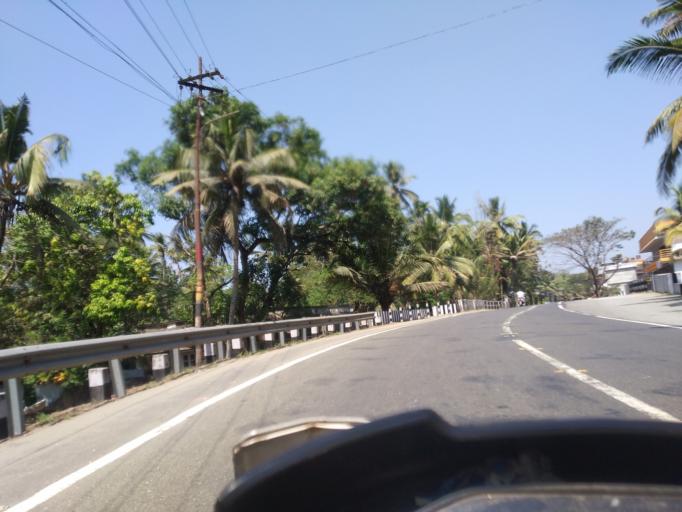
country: IN
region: Kerala
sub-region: Thrissur District
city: Kodungallur
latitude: 10.1701
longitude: 76.2122
